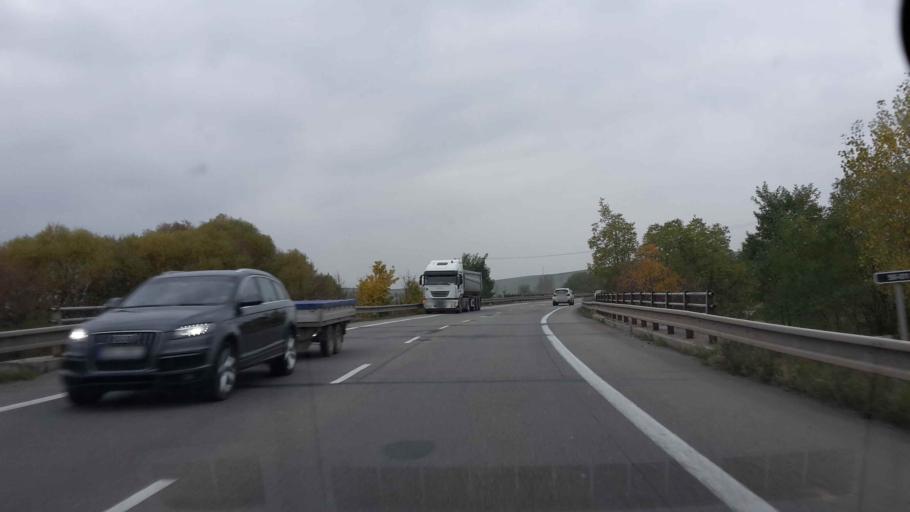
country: CZ
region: South Moravian
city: Slavkov u Brna
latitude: 49.1460
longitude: 16.8703
